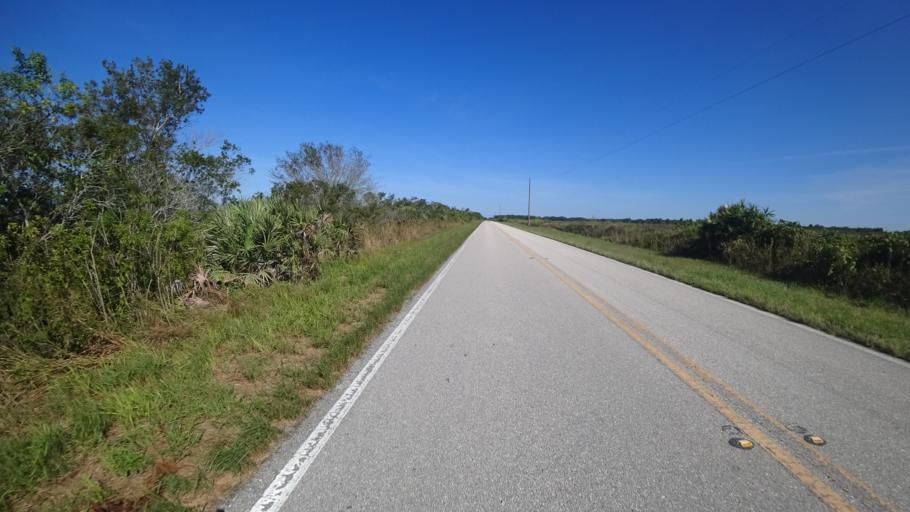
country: US
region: Florida
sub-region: Hillsborough County
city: Wimauma
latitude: 27.6064
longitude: -82.2928
